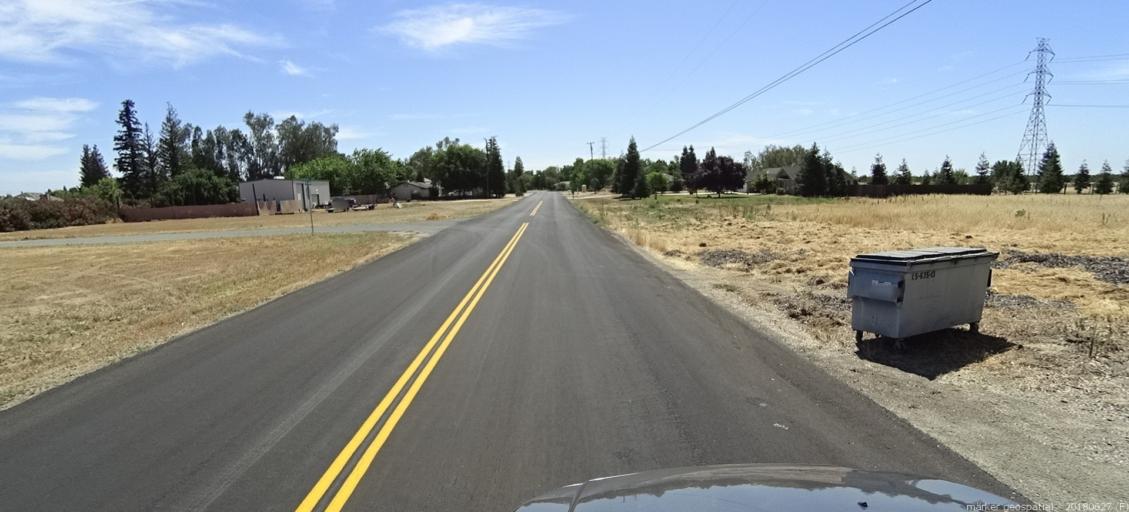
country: US
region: California
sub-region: Madera County
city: Bonadelle Ranchos-Madera Ranchos
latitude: 36.9179
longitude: -119.8839
